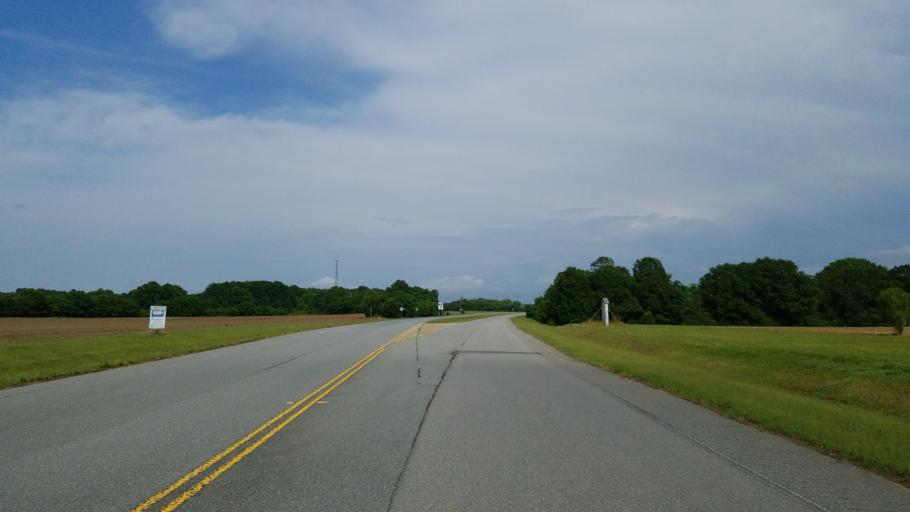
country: US
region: Georgia
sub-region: Houston County
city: Perry
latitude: 32.4360
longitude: -83.7726
